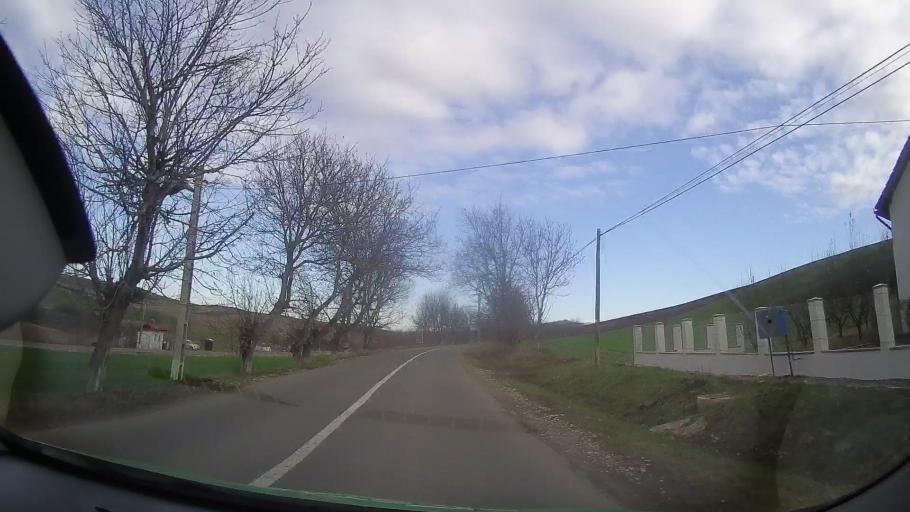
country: RO
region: Mures
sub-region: Comuna Iclanzel
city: Iclanzel
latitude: 46.5053
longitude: 24.2571
